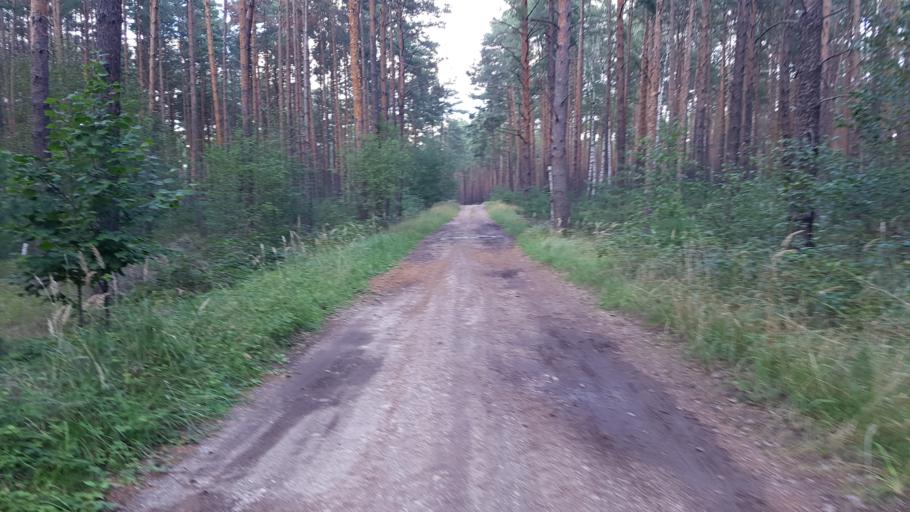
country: DE
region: Brandenburg
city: Sonnewalde
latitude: 51.6395
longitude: 13.6490
